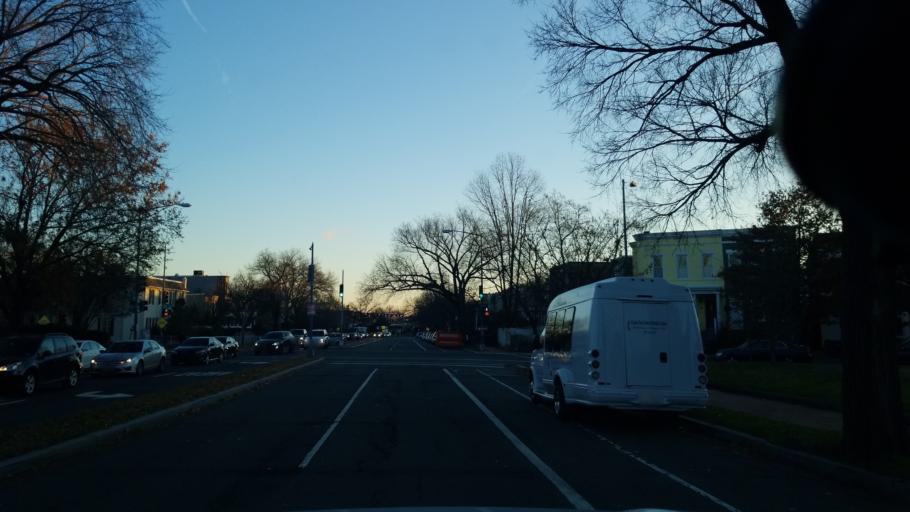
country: US
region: Washington, D.C.
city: Washington, D.C.
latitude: 38.8922
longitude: -76.9842
